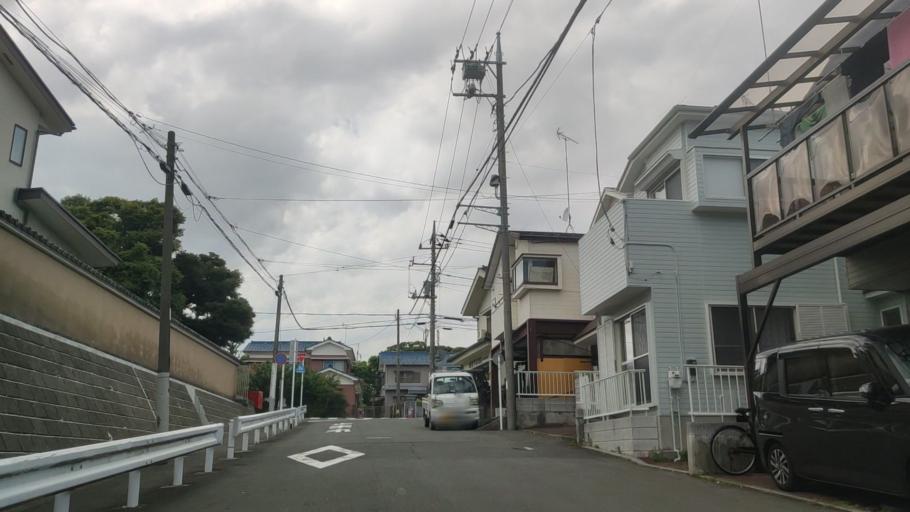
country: JP
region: Kanagawa
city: Yokohama
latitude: 35.4283
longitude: 139.6307
